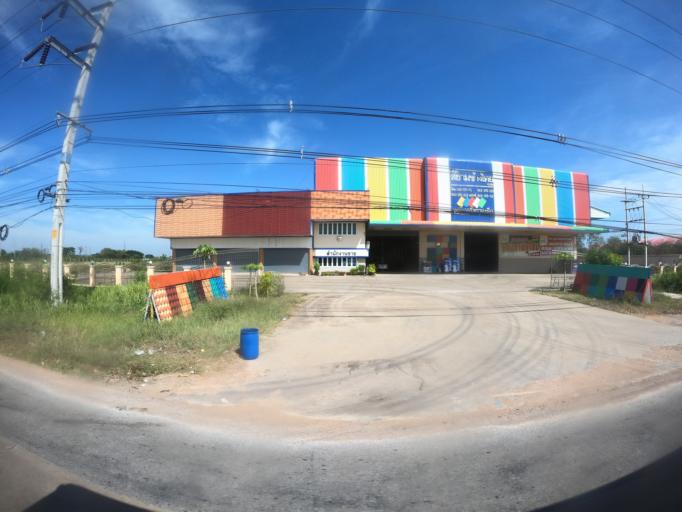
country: TH
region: Khon Kaen
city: Khon Kaen
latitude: 16.4377
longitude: 102.9216
